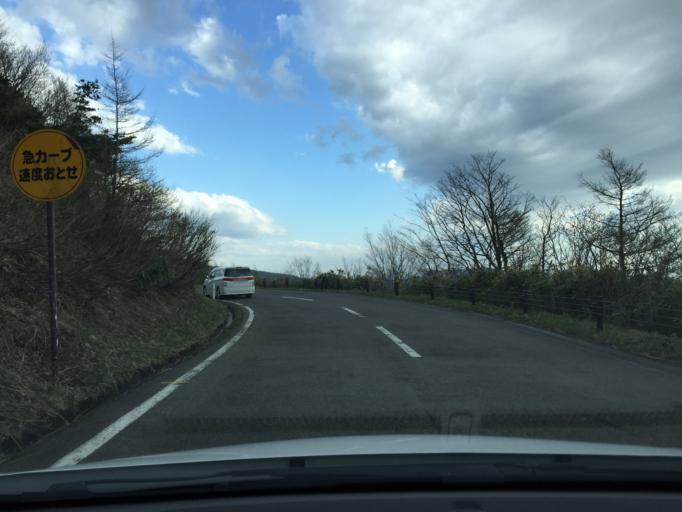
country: JP
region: Fukushima
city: Inawashiro
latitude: 37.6713
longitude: 140.2490
